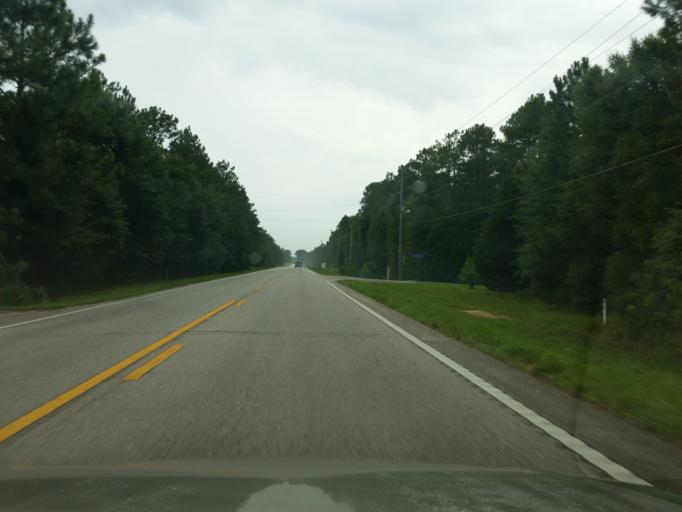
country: US
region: Alabama
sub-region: Baldwin County
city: Elberta
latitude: 30.5168
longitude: -87.4784
